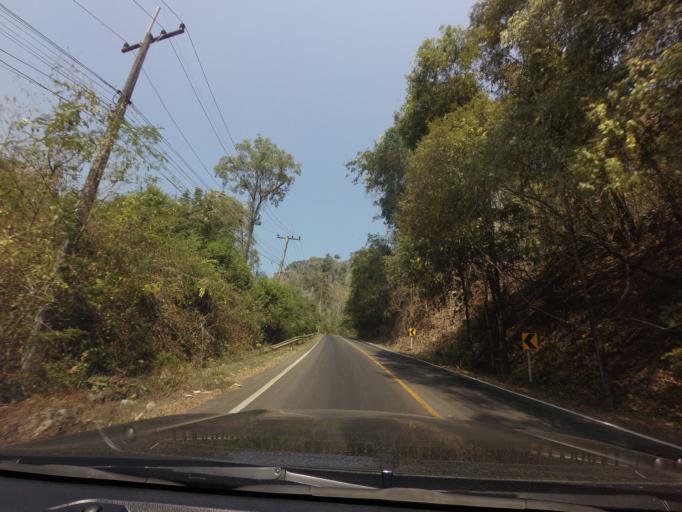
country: TH
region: Kanchanaburi
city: Thong Pha Phum
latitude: 14.7777
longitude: 98.5786
